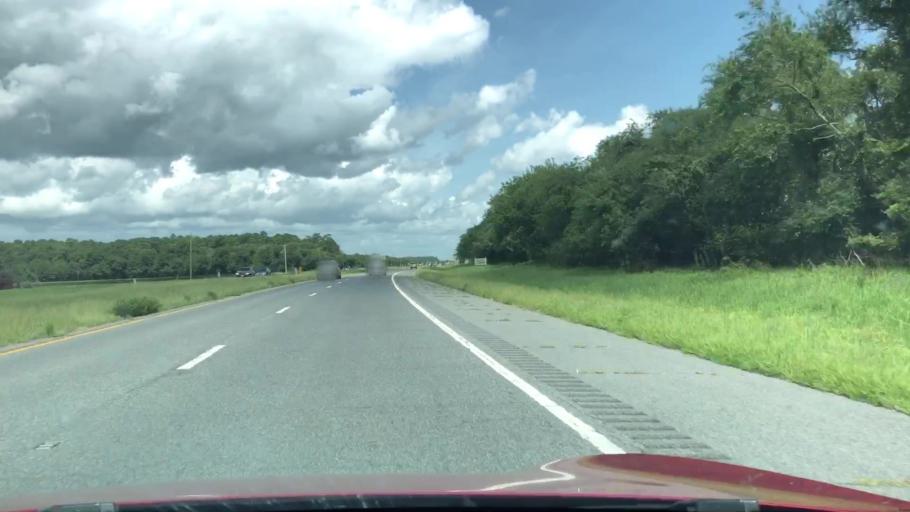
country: US
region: Virginia
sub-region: Northampton County
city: Cape Charles
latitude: 37.1502
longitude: -75.9715
